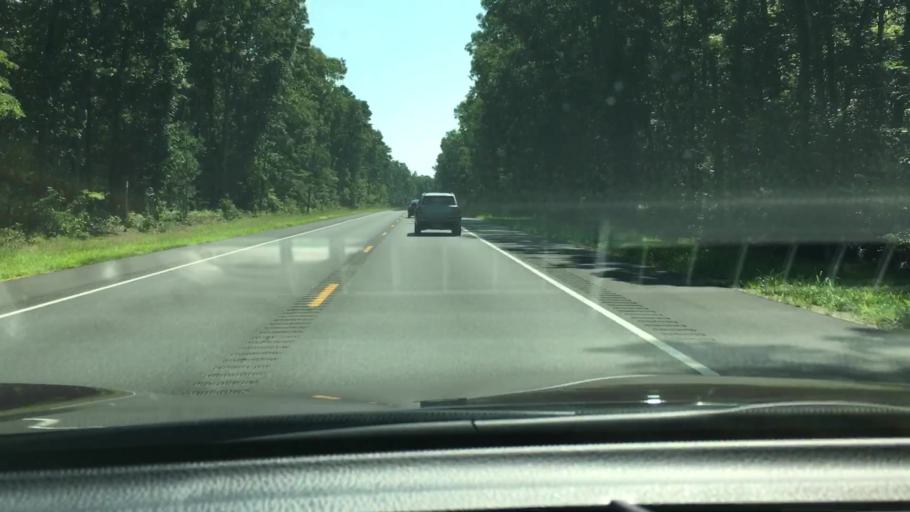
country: US
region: New Jersey
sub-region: Cape May County
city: Woodbine
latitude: 39.3168
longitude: -74.8390
